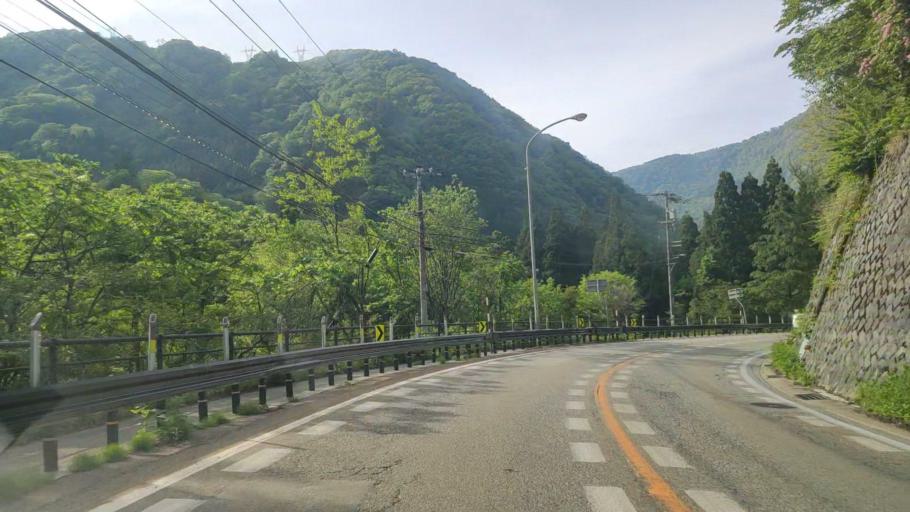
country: JP
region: Toyama
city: Yatsuomachi-higashikumisaka
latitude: 36.4367
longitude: 137.2737
